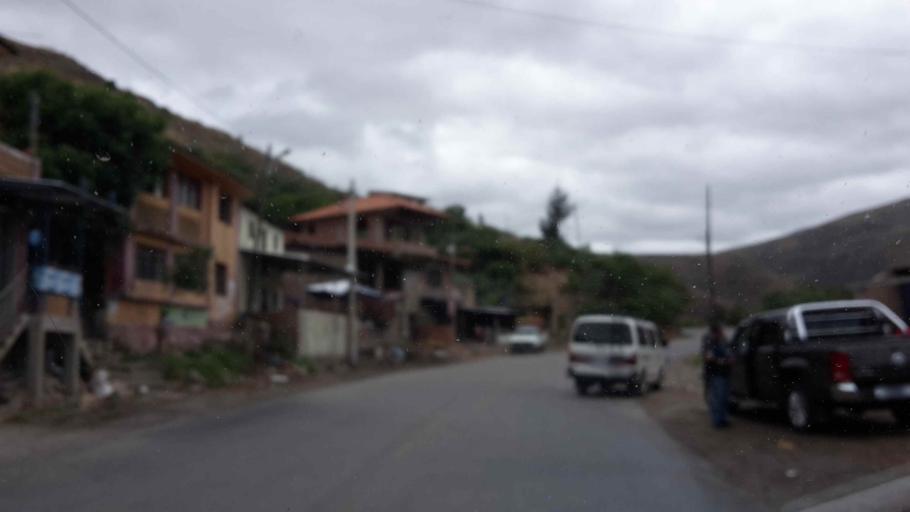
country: BO
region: Cochabamba
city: Punata
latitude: -17.5090
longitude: -65.8069
